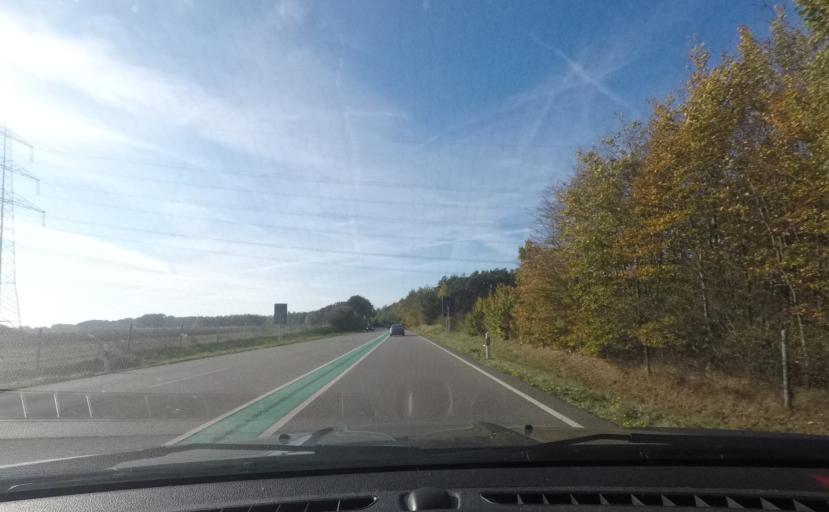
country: DE
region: North Rhine-Westphalia
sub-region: Regierungsbezirk Munster
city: Heiden
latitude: 51.8584
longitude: 6.9619
